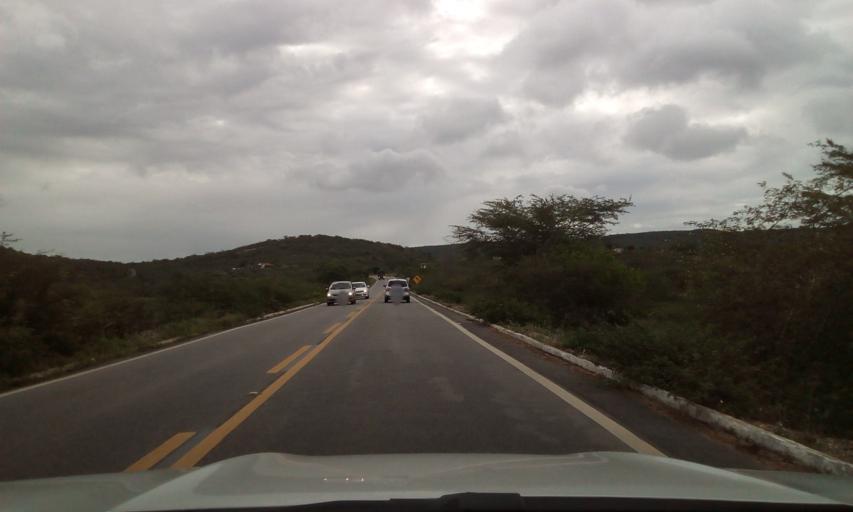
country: BR
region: Paraiba
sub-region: Cuite
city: Cuite
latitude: -6.6783
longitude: -36.0859
